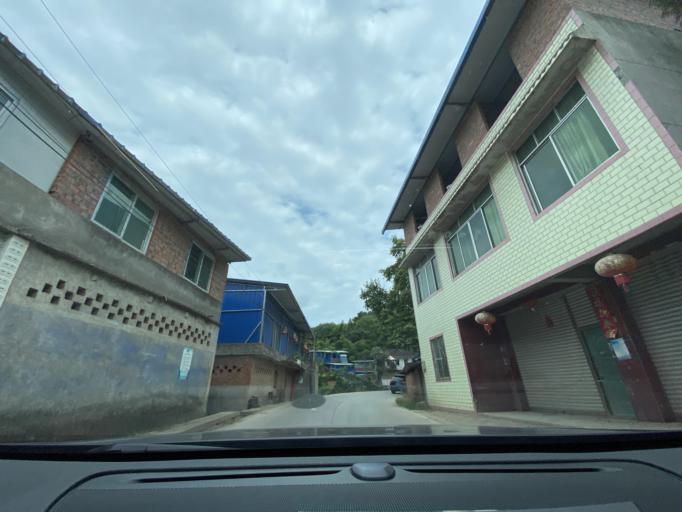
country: CN
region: Sichuan
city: Jiancheng
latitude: 30.4416
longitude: 104.5427
